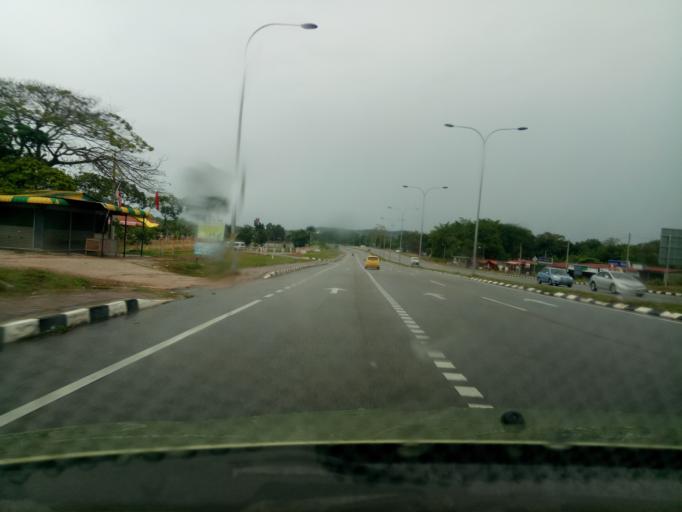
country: MY
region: Kedah
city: Sungai Petani
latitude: 5.6246
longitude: 100.5345
